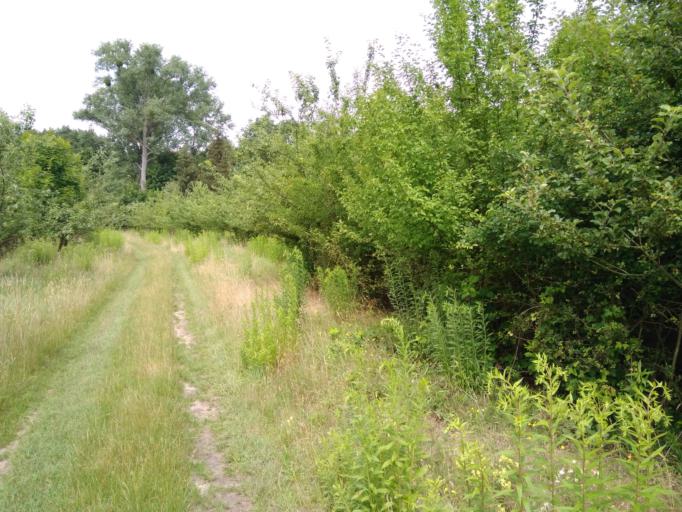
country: DE
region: Brandenburg
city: Grossbeeren
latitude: 52.3293
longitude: 13.3193
